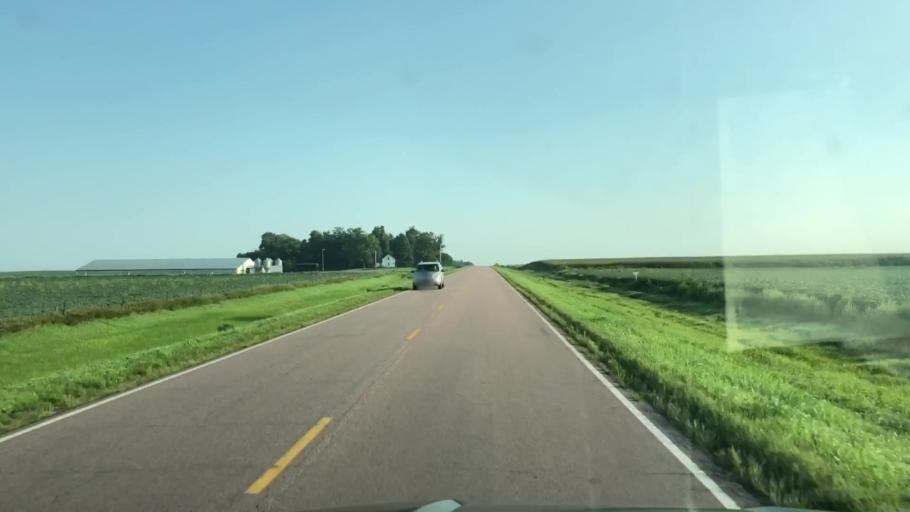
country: US
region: Iowa
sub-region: Lyon County
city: George
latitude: 43.2783
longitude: -95.9997
